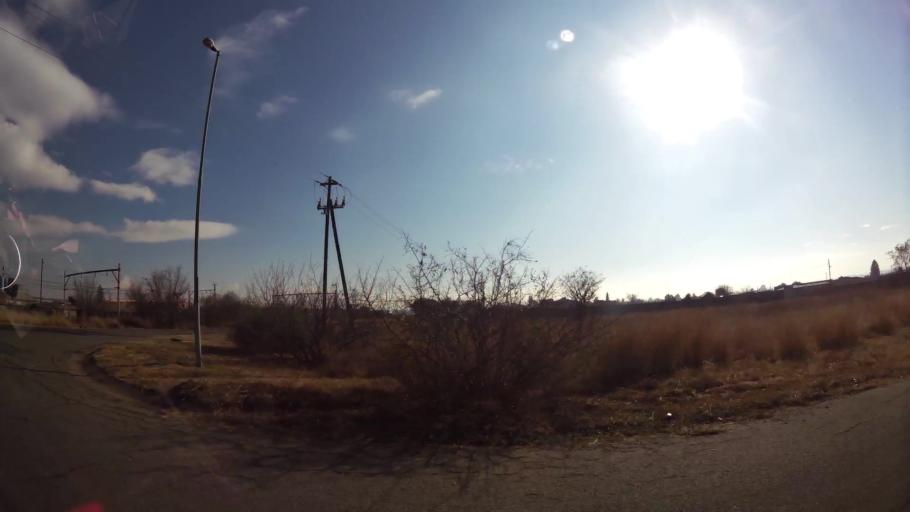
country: ZA
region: Gauteng
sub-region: Sedibeng District Municipality
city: Meyerton
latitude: -26.5052
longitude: 28.0567
